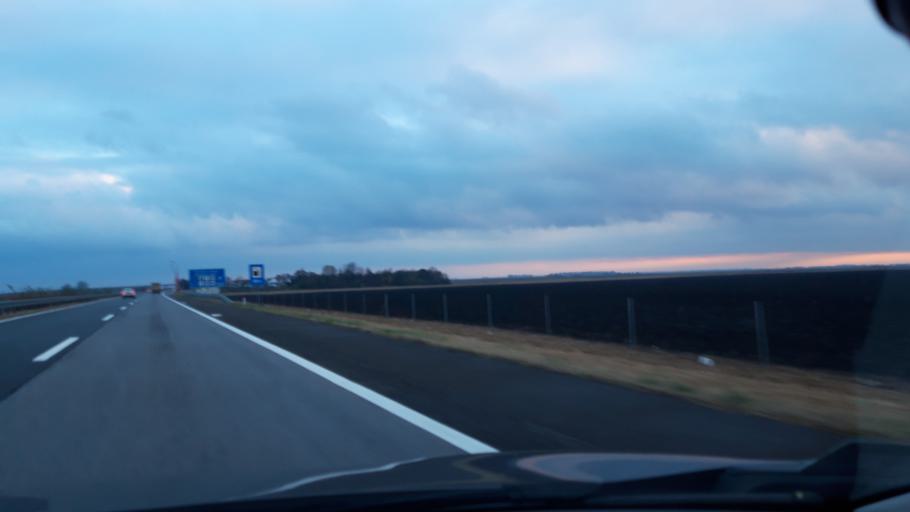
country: RS
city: Zmajevo
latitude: 45.5130
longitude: 19.7234
